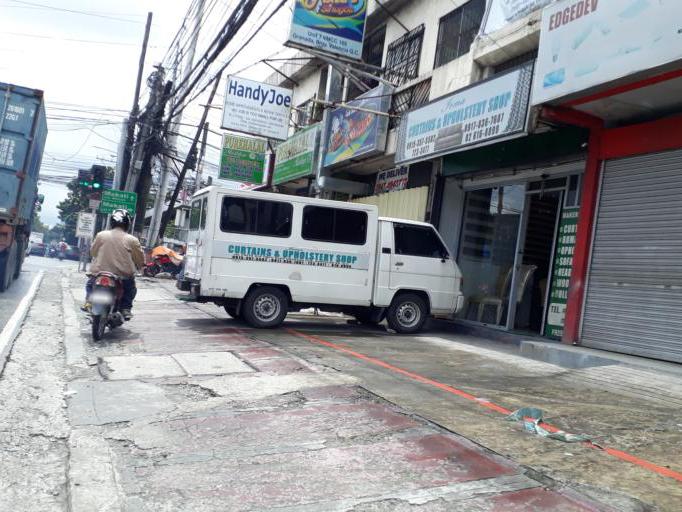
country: PH
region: Metro Manila
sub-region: San Juan
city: San Juan
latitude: 14.6081
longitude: 121.0388
